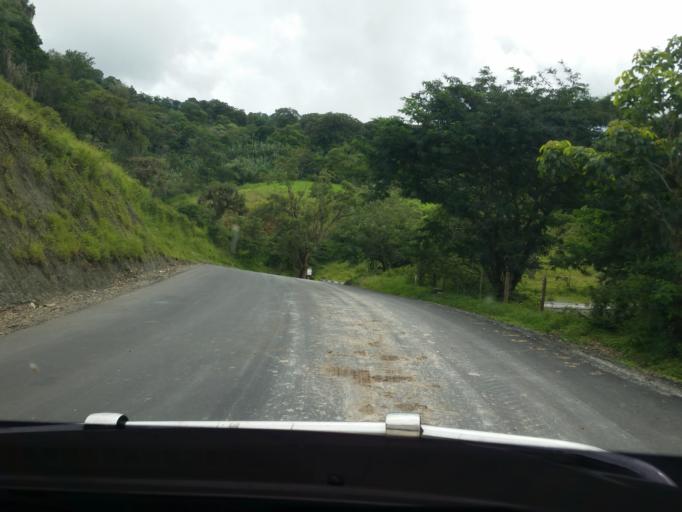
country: NI
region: Jinotega
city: Jinotega
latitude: 13.1657
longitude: -85.9242
